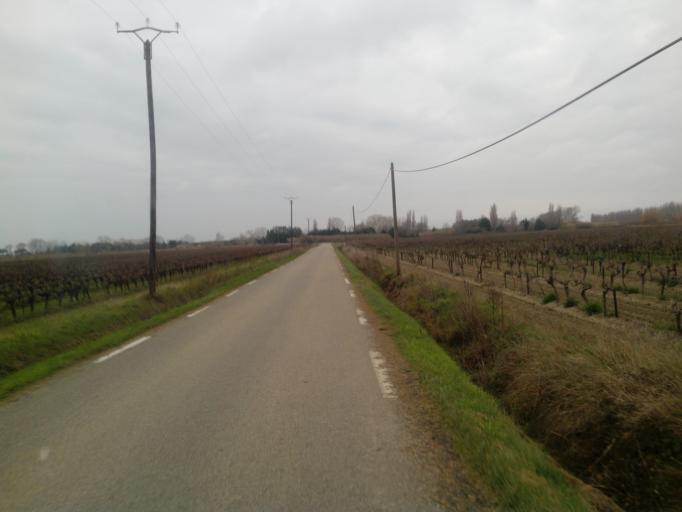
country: FR
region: Languedoc-Roussillon
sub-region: Departement du Gard
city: Saint-Gilles
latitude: 43.5837
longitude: 4.3450
